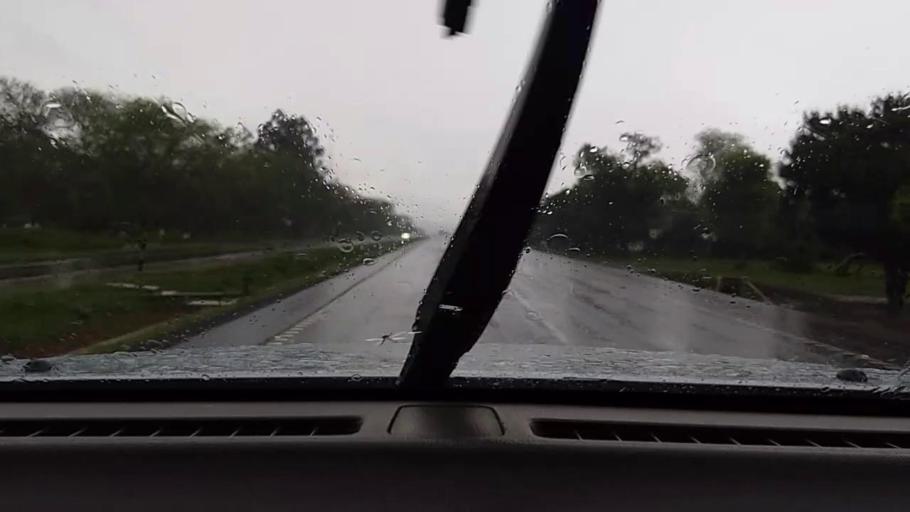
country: PY
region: Caaguazu
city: Repatriacion
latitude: -25.4516
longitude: -55.9030
